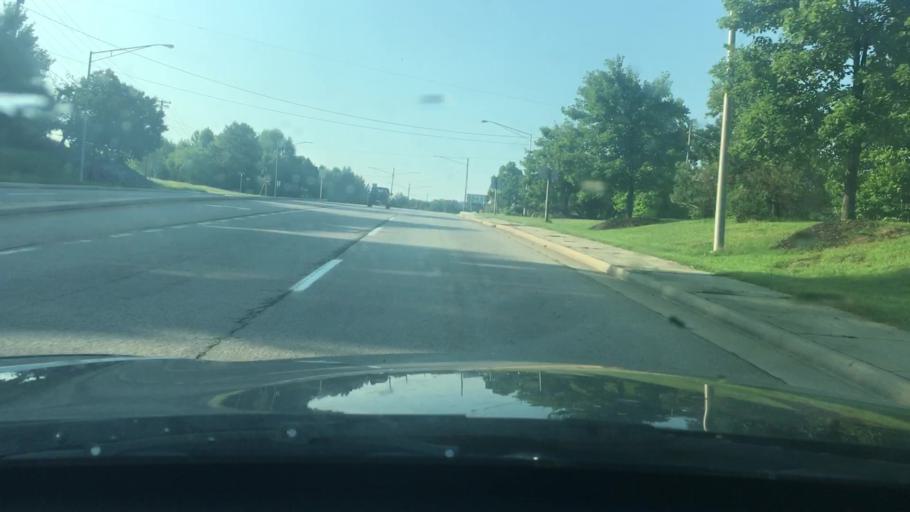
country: US
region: Virginia
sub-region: City of Danville
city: Danville
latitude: 36.5507
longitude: -79.4011
